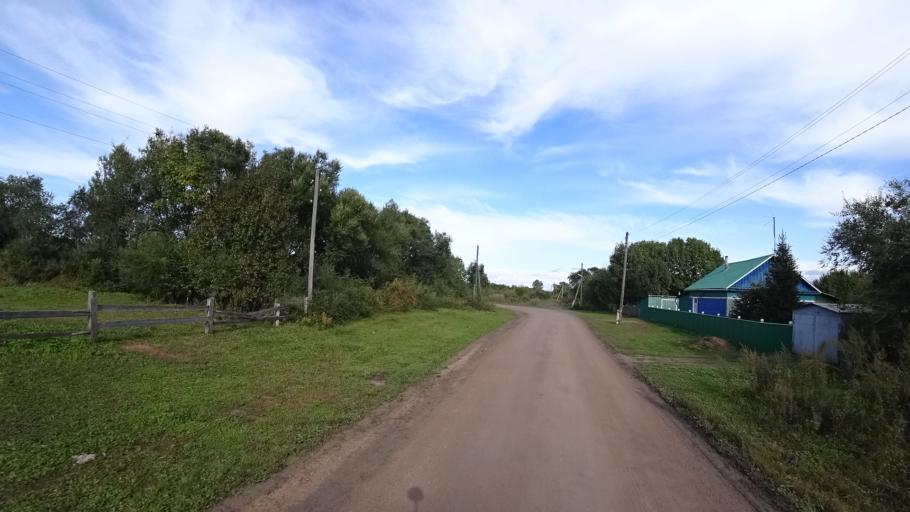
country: RU
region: Amur
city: Arkhara
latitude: 49.3522
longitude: 130.1066
